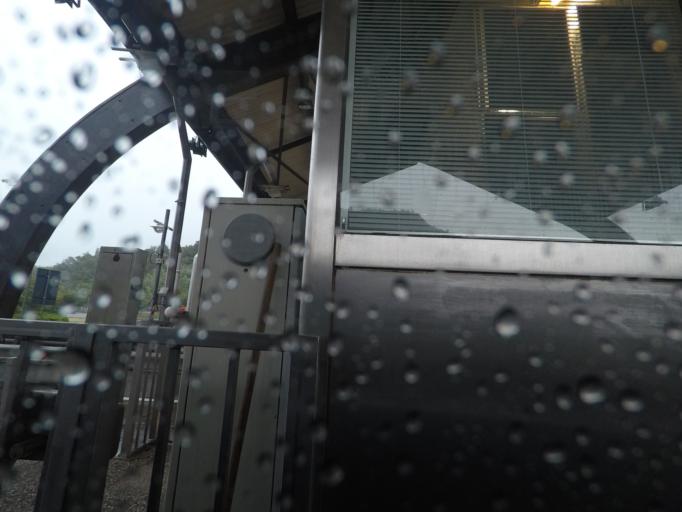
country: IT
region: Aosta Valley
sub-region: Valle d'Aosta
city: Aymavilles
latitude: 45.7089
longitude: 7.2469
